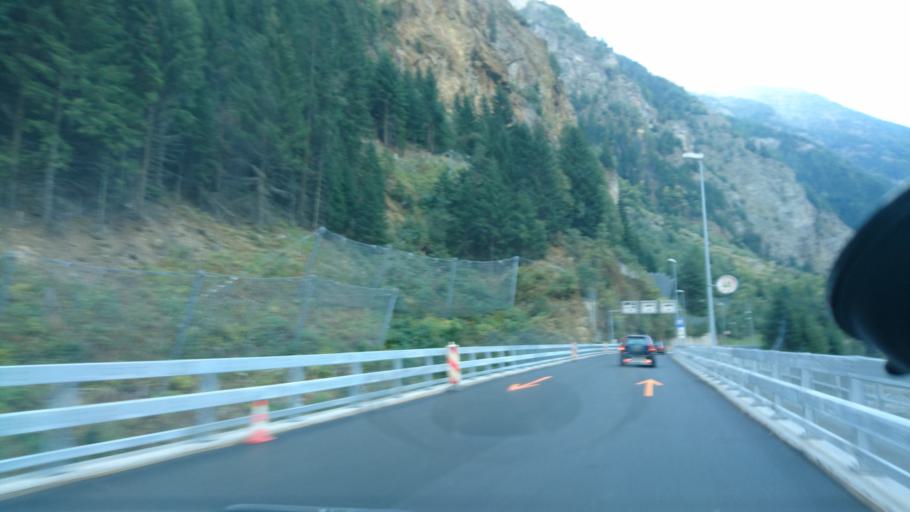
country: CH
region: Valais
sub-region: Leuk District
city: Gampel
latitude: 46.3663
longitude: 7.7561
